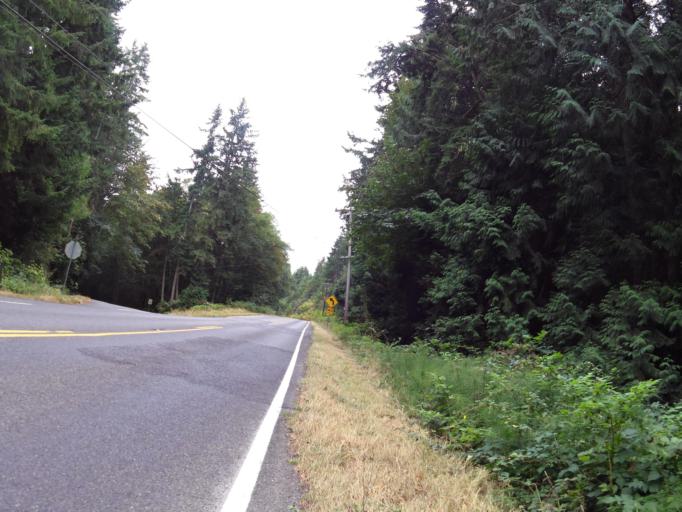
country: US
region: Washington
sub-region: Jefferson County
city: Port Hadlock-Irondale
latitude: 48.0113
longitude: -122.7297
